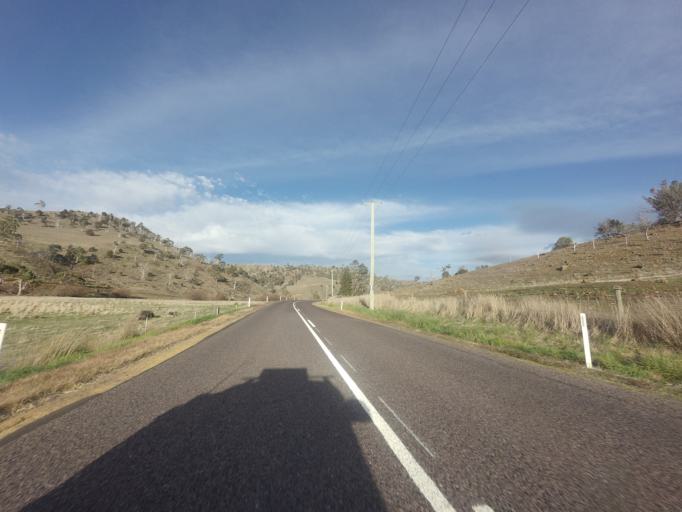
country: AU
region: Tasmania
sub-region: Brighton
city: Bridgewater
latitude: -42.4355
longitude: 147.1456
